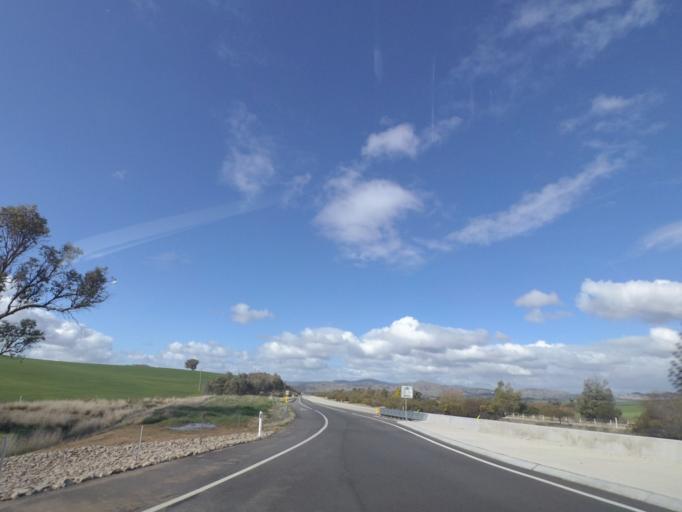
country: AU
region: New South Wales
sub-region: Albury Municipality
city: Lavington
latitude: -35.9153
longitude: 147.1039
